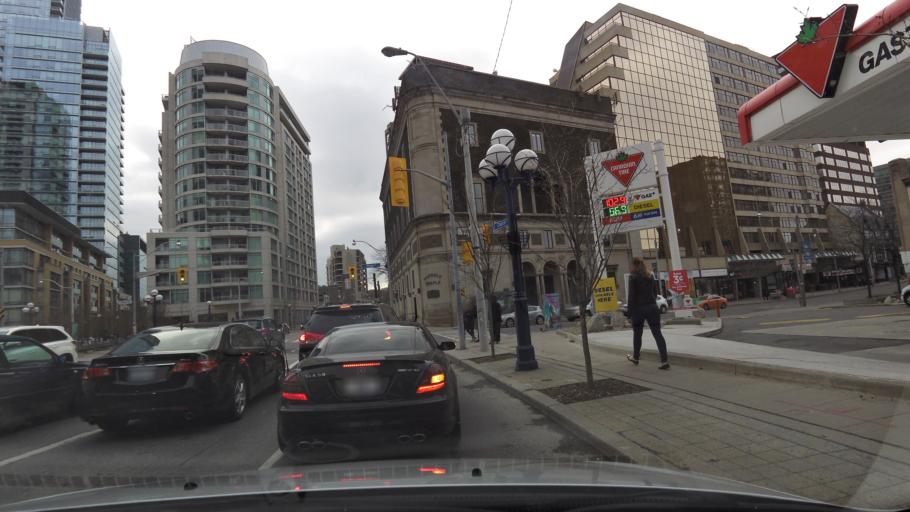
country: CA
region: Ontario
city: Toronto
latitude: 43.6729
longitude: -79.3875
